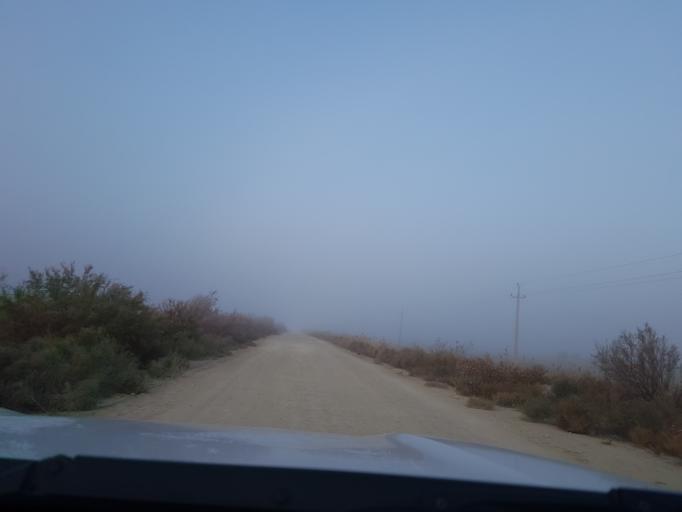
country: TM
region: Dasoguz
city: Koeneuergench
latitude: 41.8451
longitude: 58.4574
